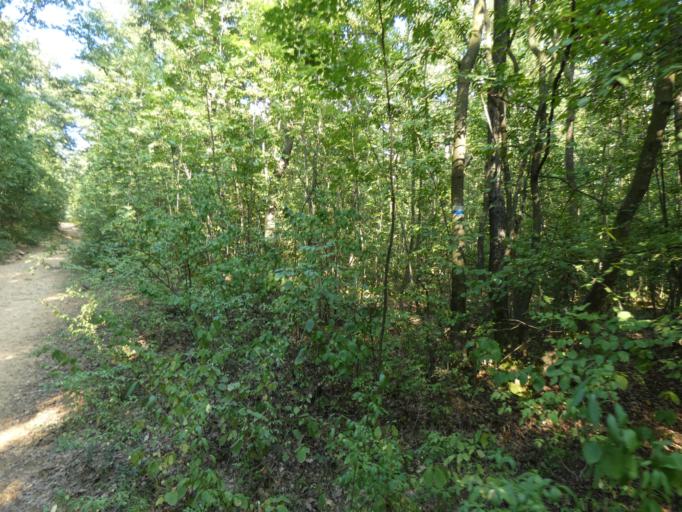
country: HU
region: Pest
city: Pilisborosjeno
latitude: 47.6191
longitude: 18.9769
